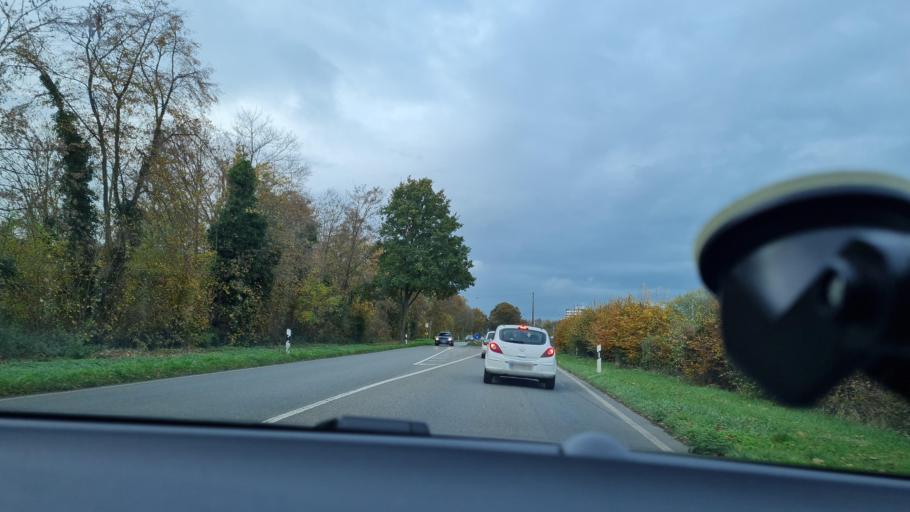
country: DE
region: North Rhine-Westphalia
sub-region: Regierungsbezirk Dusseldorf
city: Voerde
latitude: 51.6249
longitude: 6.6678
